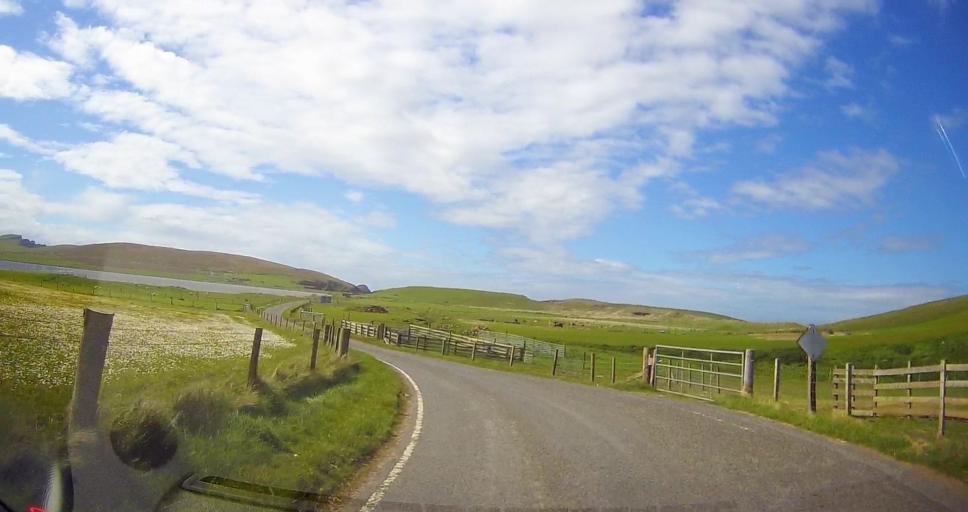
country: GB
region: Scotland
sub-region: Shetland Islands
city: Sandwick
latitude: 59.9412
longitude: -1.3287
